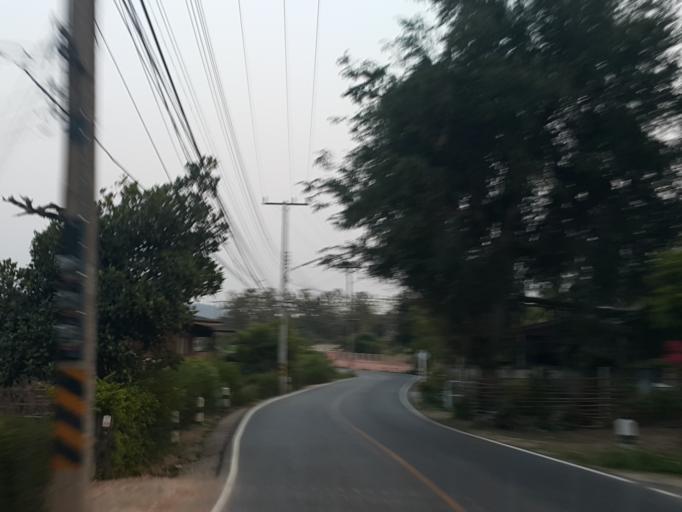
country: TH
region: Chiang Mai
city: Mae Taeng
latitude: 19.0204
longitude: 98.8761
